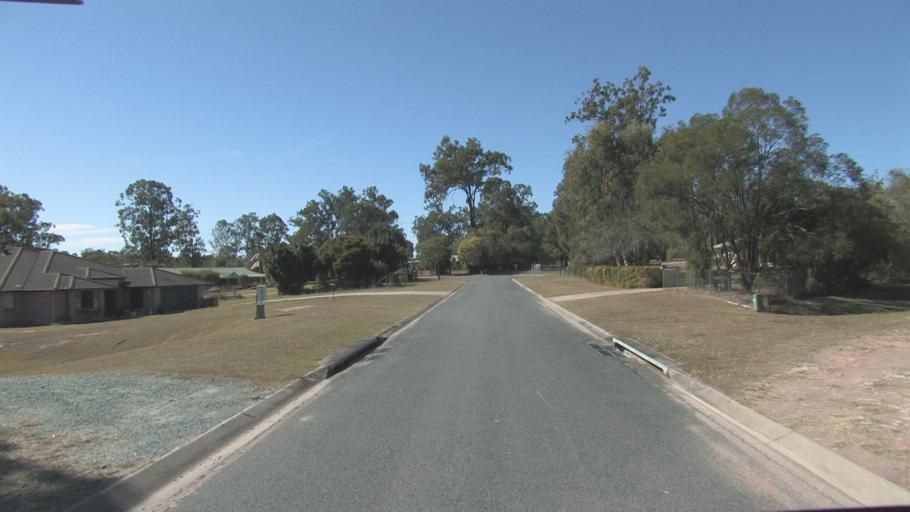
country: AU
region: Queensland
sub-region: Logan
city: North Maclean
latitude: -27.8190
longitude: 152.9550
